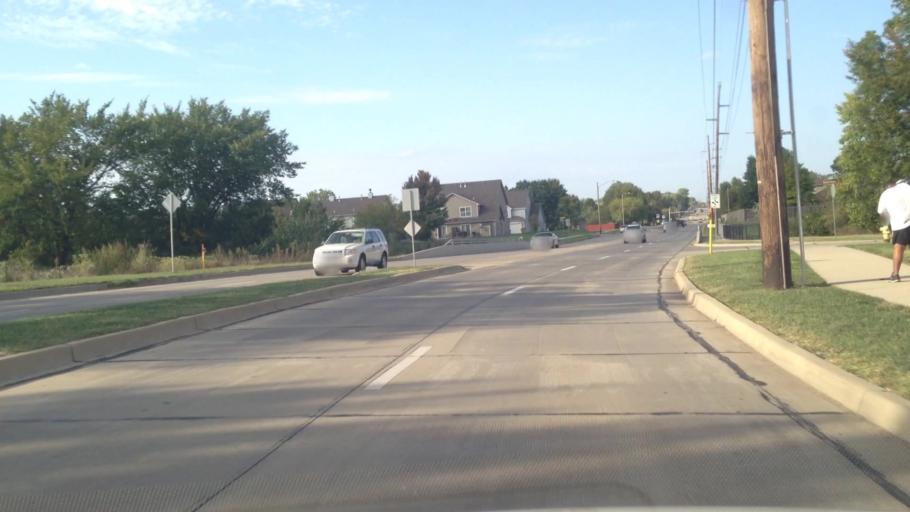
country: US
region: Kansas
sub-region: Douglas County
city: Lawrence
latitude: 38.9295
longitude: -95.2791
